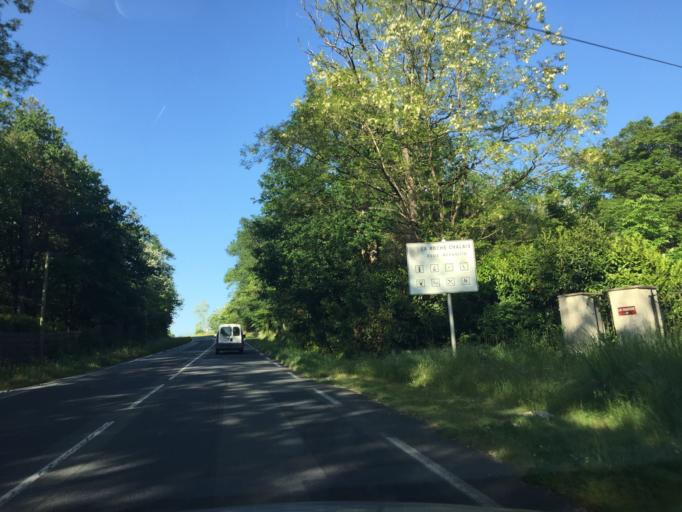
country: FR
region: Aquitaine
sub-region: Departement de la Dordogne
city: La Roche-Chalais
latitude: 45.1436
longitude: 0.0016
